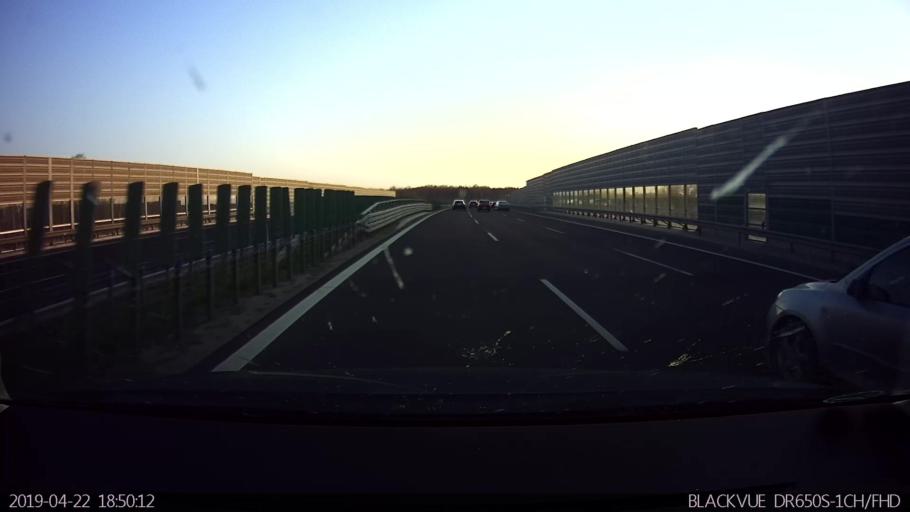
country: PL
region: Masovian Voivodeship
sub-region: Powiat wolominski
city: Kobylka
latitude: 52.3592
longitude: 21.1847
